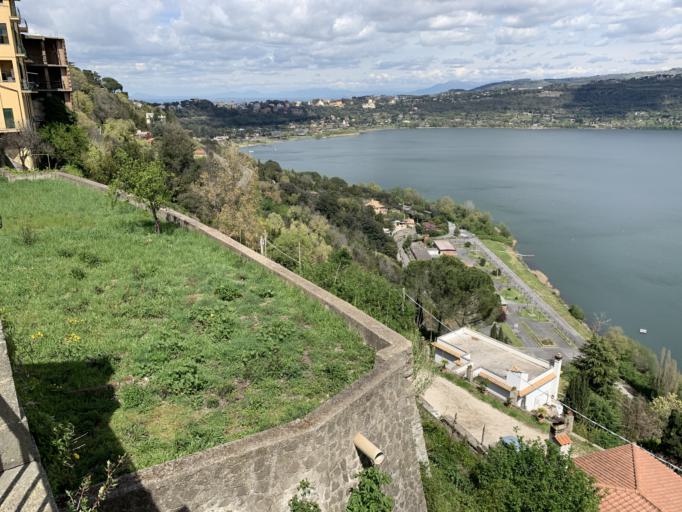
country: IT
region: Latium
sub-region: Citta metropolitana di Roma Capitale
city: Castel Gandolfo
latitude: 41.7430
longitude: 12.6528
